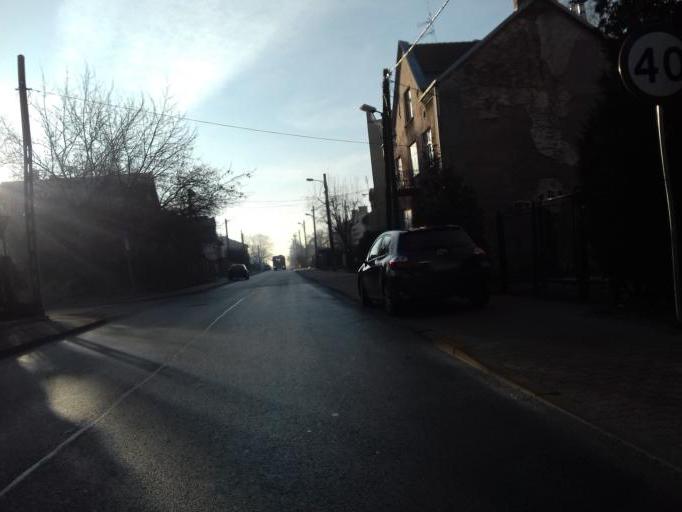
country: PL
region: Lesser Poland Voivodeship
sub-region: Krakow
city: Krakow
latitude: 50.0236
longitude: 19.9422
